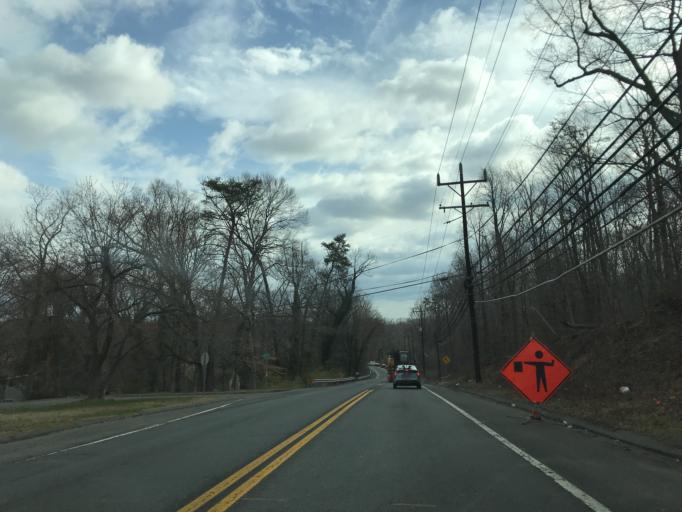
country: US
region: Maryland
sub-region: Montgomery County
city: Hillandale
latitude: 39.0294
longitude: -76.9580
